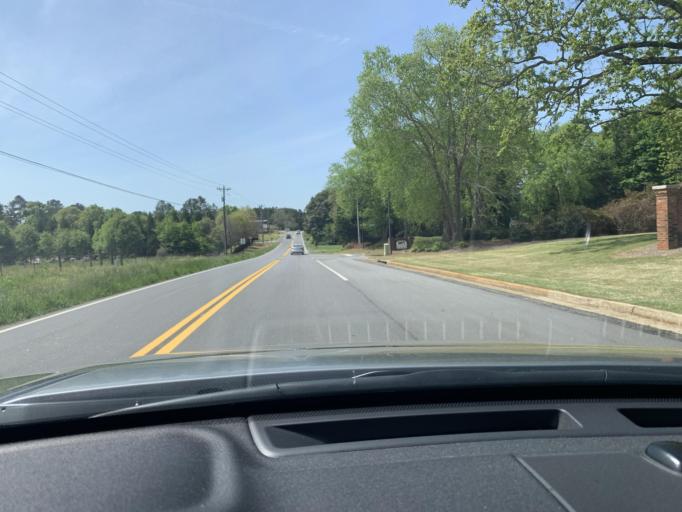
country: US
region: Georgia
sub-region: Oconee County
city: Watkinsville
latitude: 33.8829
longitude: -83.4316
